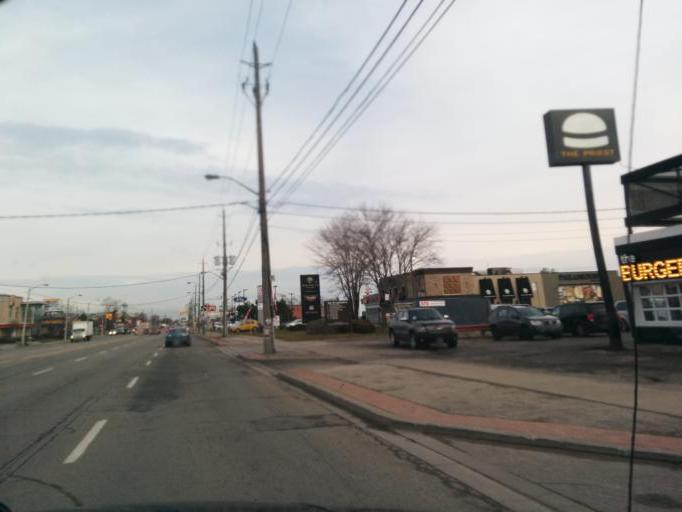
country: CA
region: Ontario
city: Etobicoke
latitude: 43.6171
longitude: -79.5431
